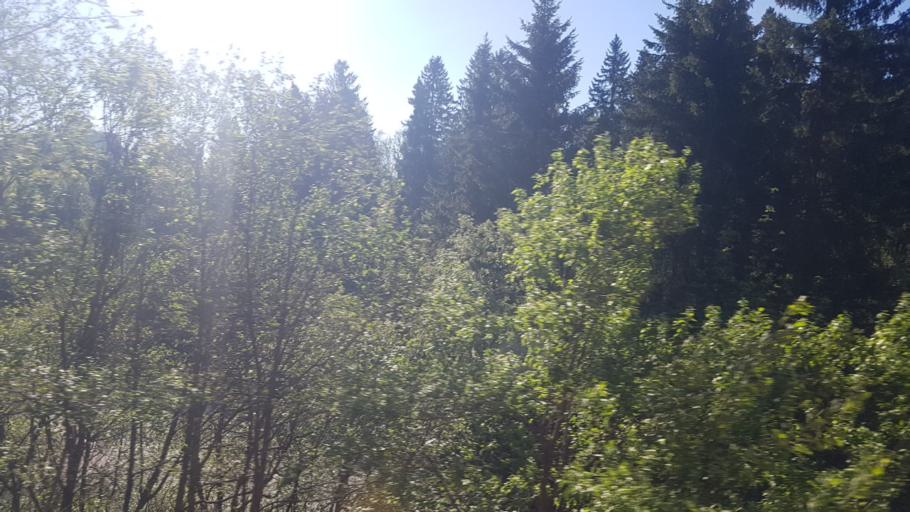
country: NO
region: Sor-Trondelag
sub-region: Trondheim
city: Trondheim
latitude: 63.3655
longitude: 10.3666
